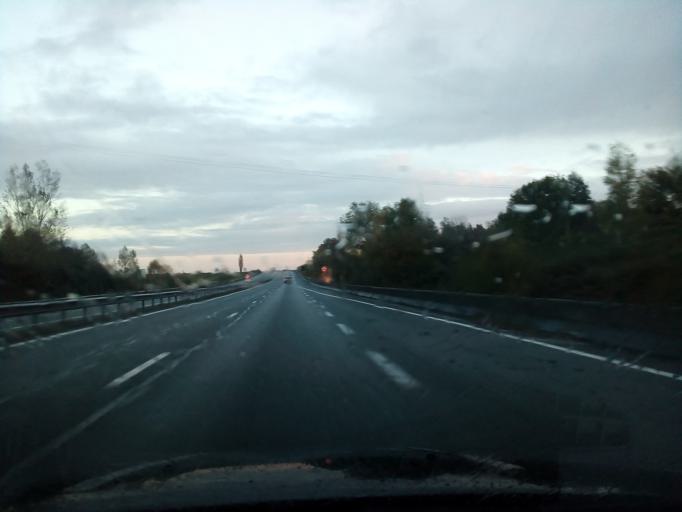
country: FR
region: Aquitaine
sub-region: Departement de la Gironde
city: Cavignac
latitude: 45.0892
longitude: -0.3822
